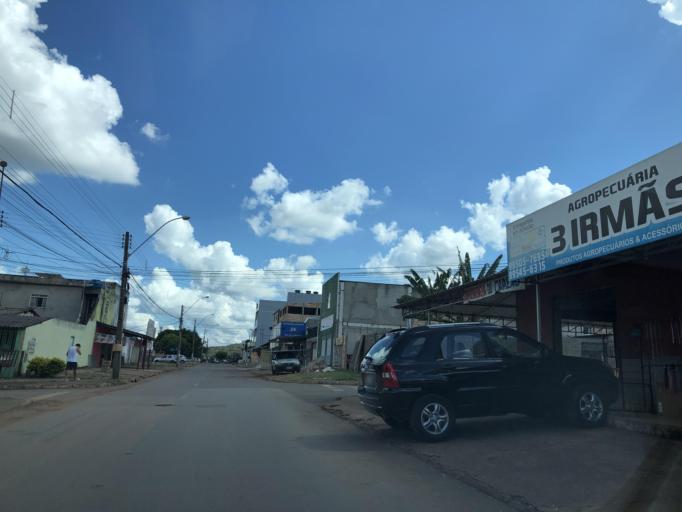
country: BR
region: Federal District
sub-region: Brasilia
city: Brasilia
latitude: -15.9007
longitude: -47.7836
